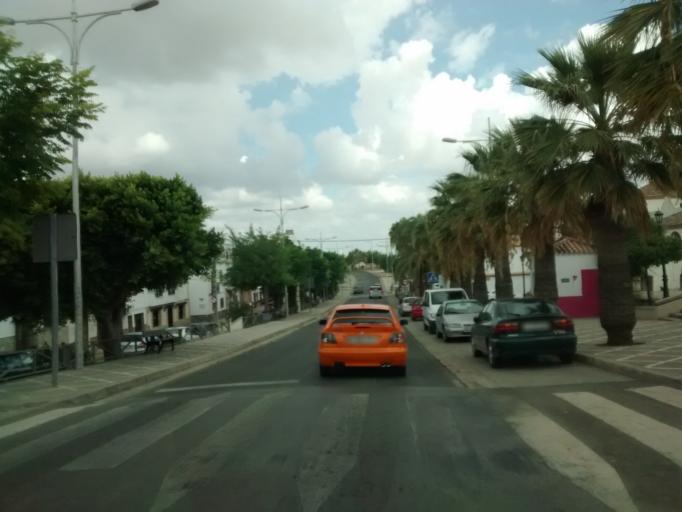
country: ES
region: Andalusia
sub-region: Provincia de Cadiz
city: Paterna de Rivera
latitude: 36.5247
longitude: -5.8672
